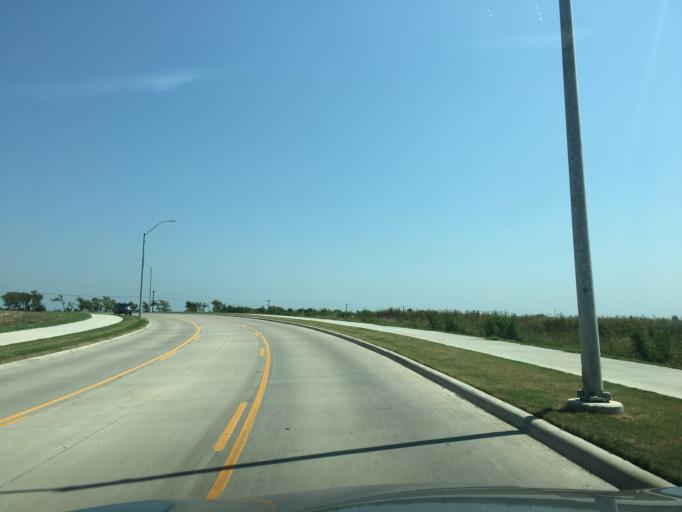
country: US
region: Texas
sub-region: Tarrant County
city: Haslet
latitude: 32.9400
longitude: -97.3199
